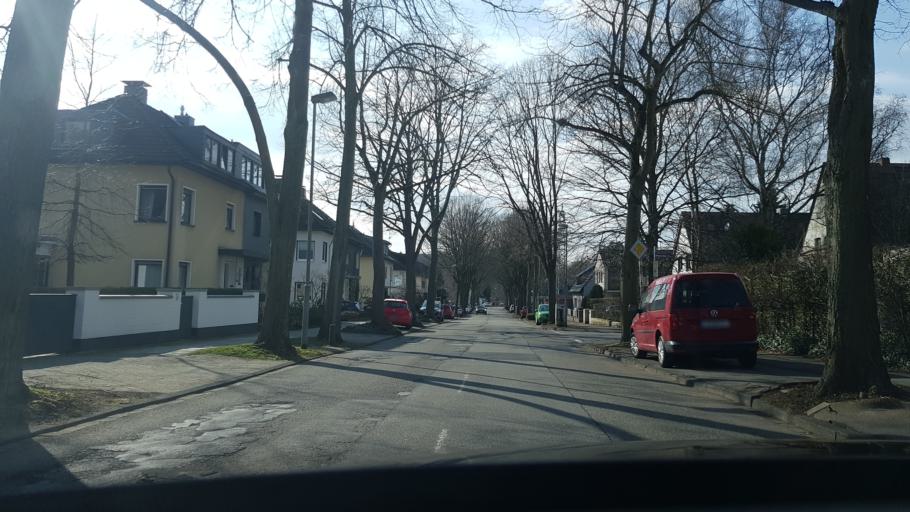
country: DE
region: North Rhine-Westphalia
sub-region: Regierungsbezirk Dusseldorf
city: Muelheim (Ruhr)
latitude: 51.4089
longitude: 6.8584
